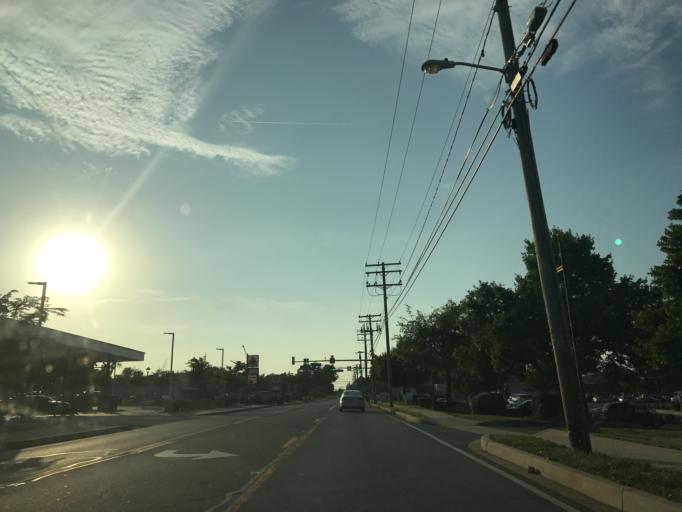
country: US
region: Maryland
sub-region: Harford County
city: Edgewood
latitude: 39.4262
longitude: -76.2980
